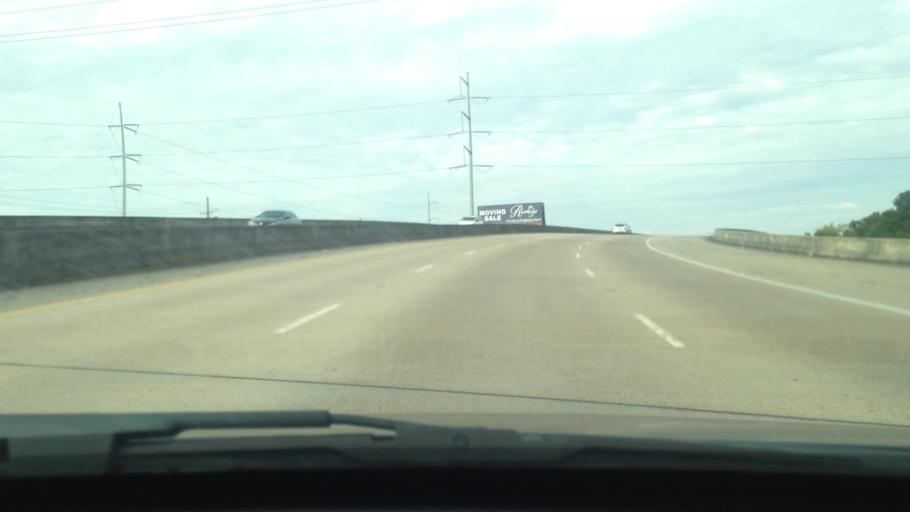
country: US
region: Louisiana
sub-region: Jefferson Parish
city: Metairie Terrace
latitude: 29.9712
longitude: -90.1606
